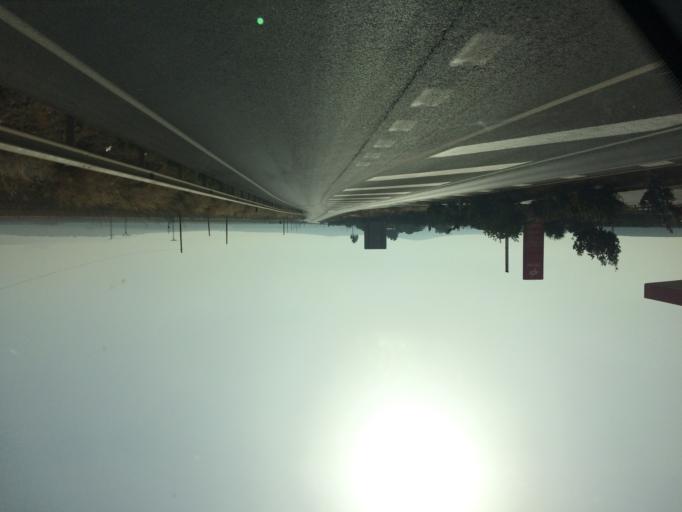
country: ES
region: Andalusia
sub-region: Provincia de Malaga
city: Humilladero
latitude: 37.0621
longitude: -4.7162
